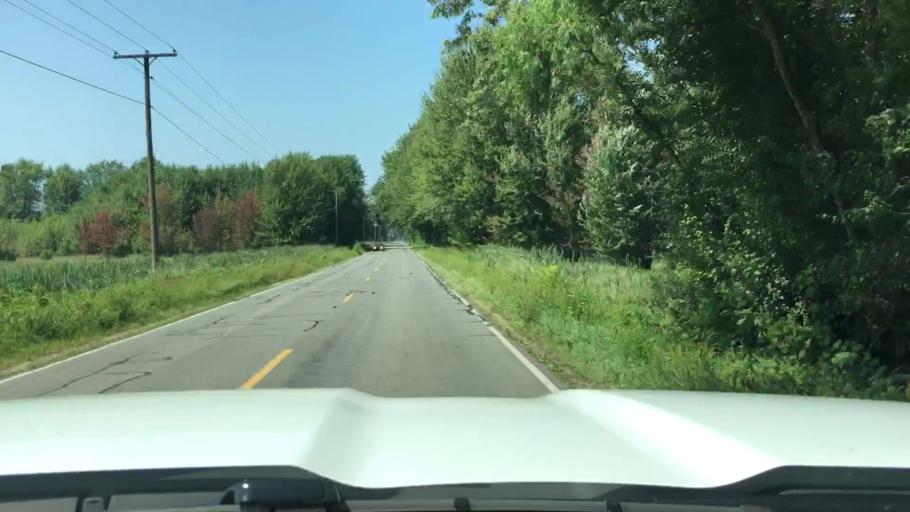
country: US
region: Michigan
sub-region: Saint Joseph County
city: Three Rivers
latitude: 41.9985
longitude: -85.6027
